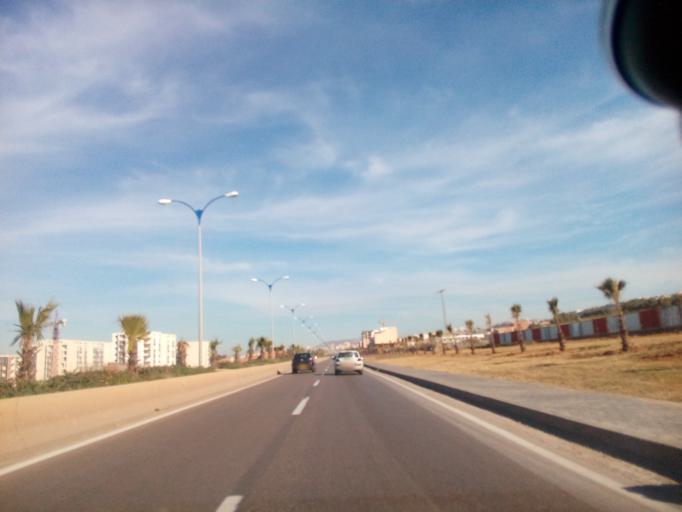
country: DZ
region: Mostaganem
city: Mostaganem
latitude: 35.9016
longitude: 0.0644
